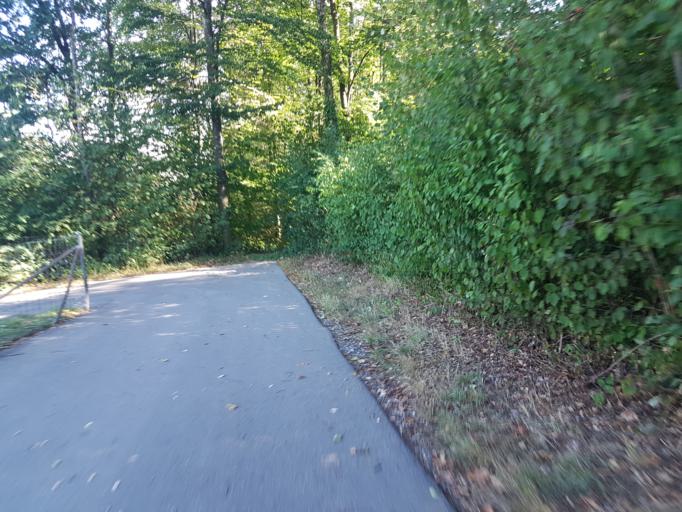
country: CH
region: Zurich
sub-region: Bezirk Pfaeffikon
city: Effretikon / Rappenhalde-Bannhalde
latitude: 47.4238
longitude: 8.6952
